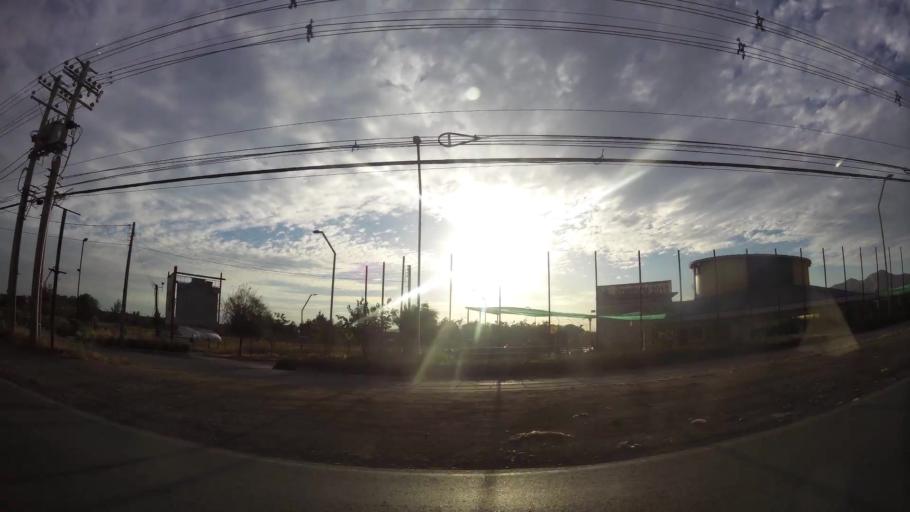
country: CL
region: Santiago Metropolitan
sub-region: Provincia de Maipo
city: San Bernardo
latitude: -33.6254
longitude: -70.6801
